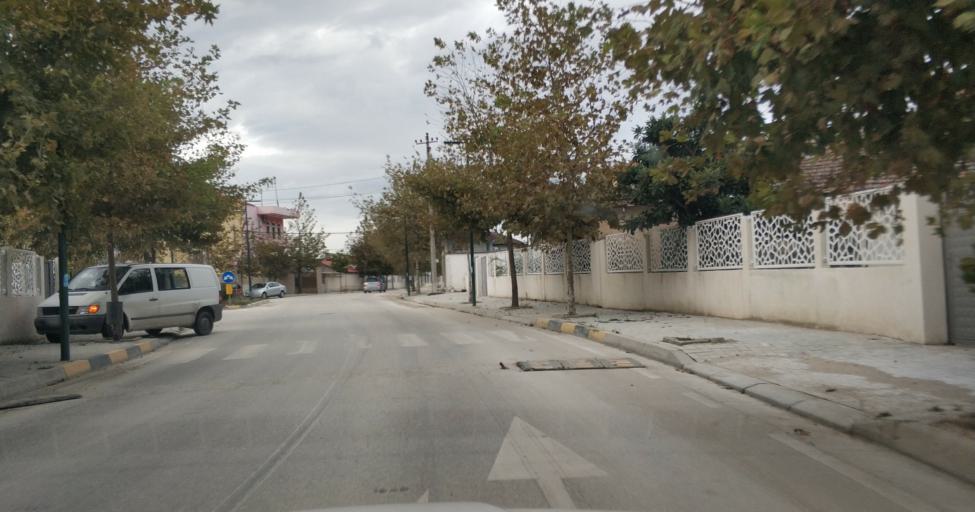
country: AL
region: Vlore
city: Vlore
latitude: 40.4465
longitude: 19.4969
